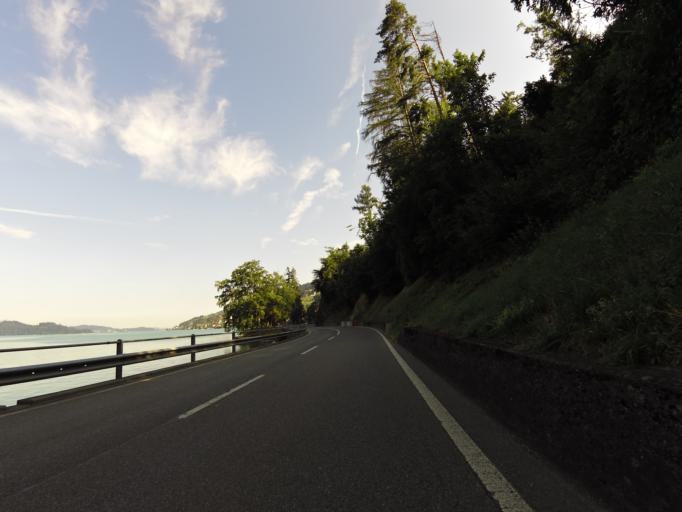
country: CH
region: Zug
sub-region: Zug
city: Walchwil
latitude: 47.0853
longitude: 8.5233
